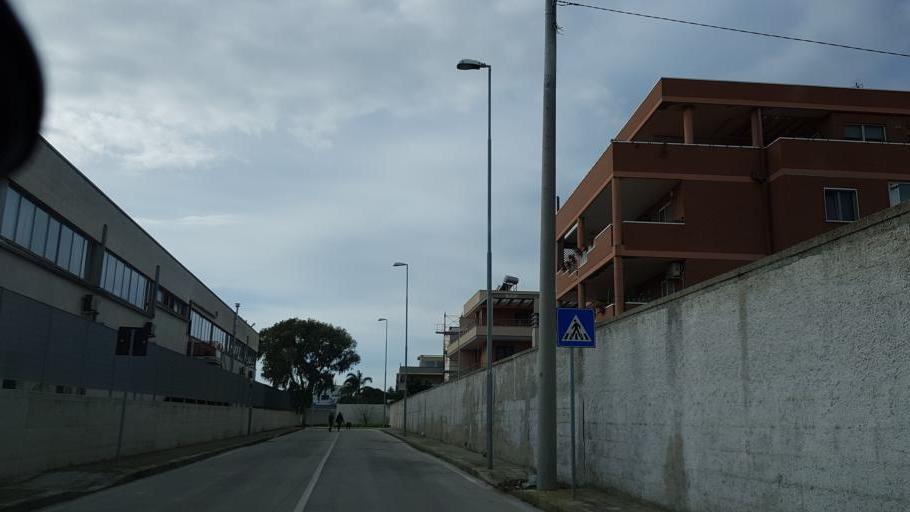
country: IT
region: Apulia
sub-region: Provincia di Brindisi
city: Materdomini
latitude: 40.6577
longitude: 17.9604
